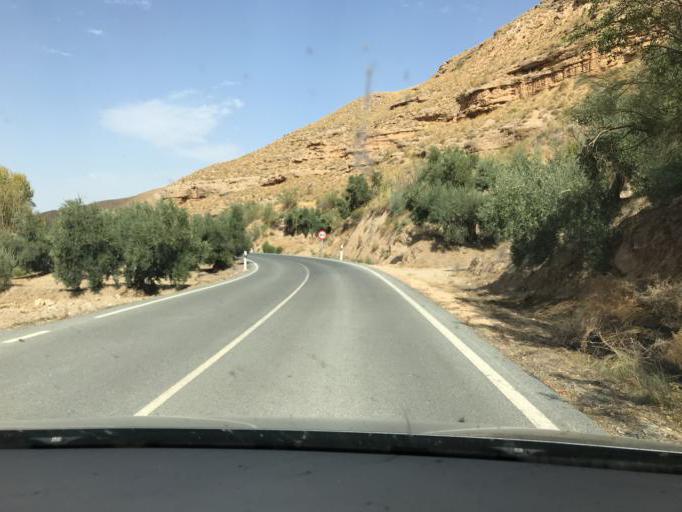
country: ES
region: Andalusia
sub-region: Provincia de Granada
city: Villanueva de las Torres
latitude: 37.4618
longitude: -3.0322
